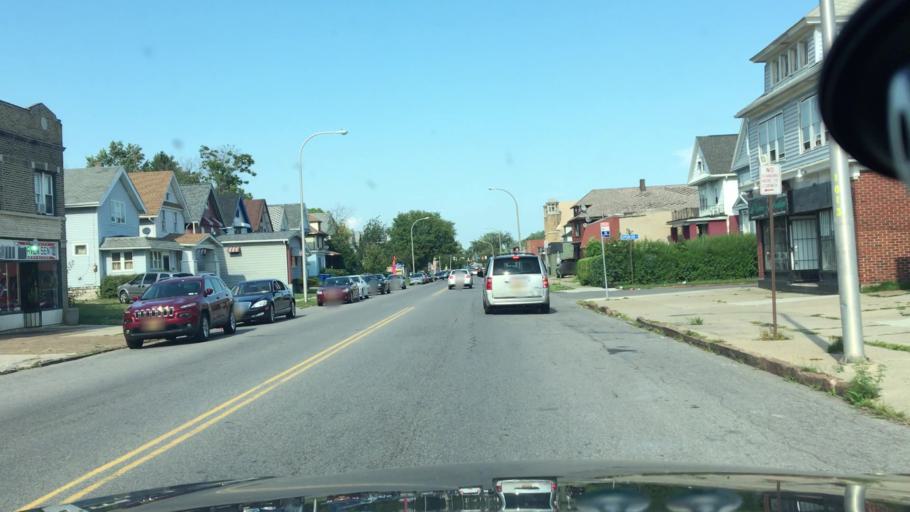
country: US
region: New York
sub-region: Erie County
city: Eggertsville
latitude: 42.9366
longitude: -78.8169
